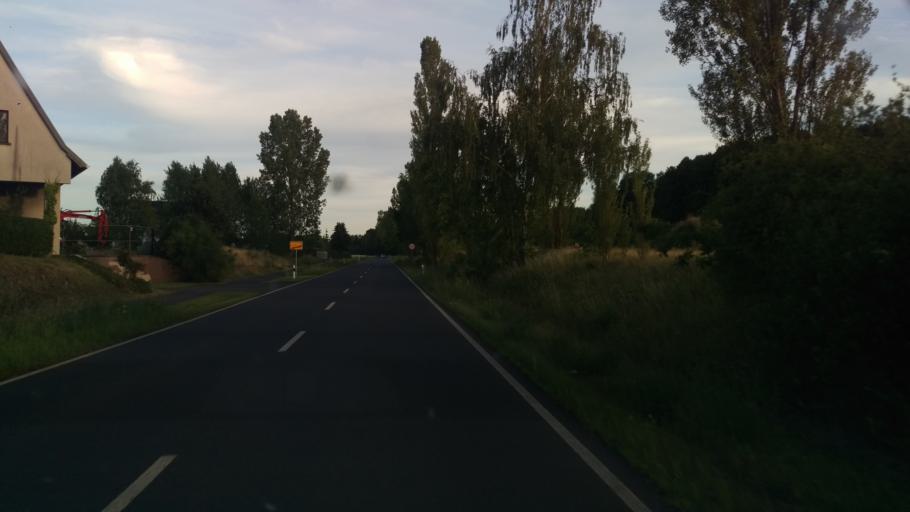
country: DE
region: Brandenburg
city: Vogelsang
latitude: 52.1789
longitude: 14.6659
